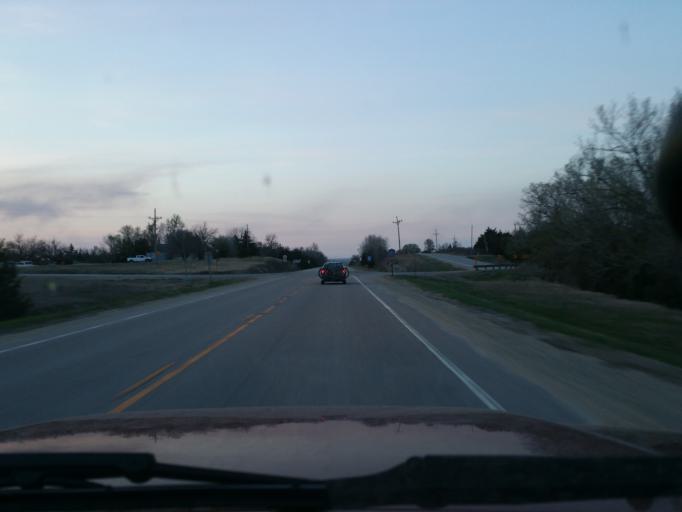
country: US
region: Kansas
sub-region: Marshall County
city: Blue Rapids
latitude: 39.4124
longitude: -96.7644
